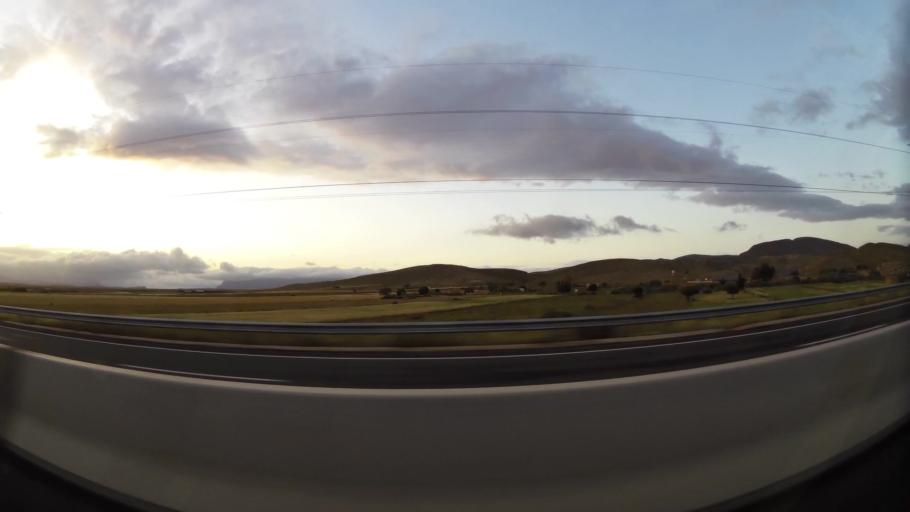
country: MA
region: Oriental
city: El Aioun
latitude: 34.5950
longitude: -2.6761
